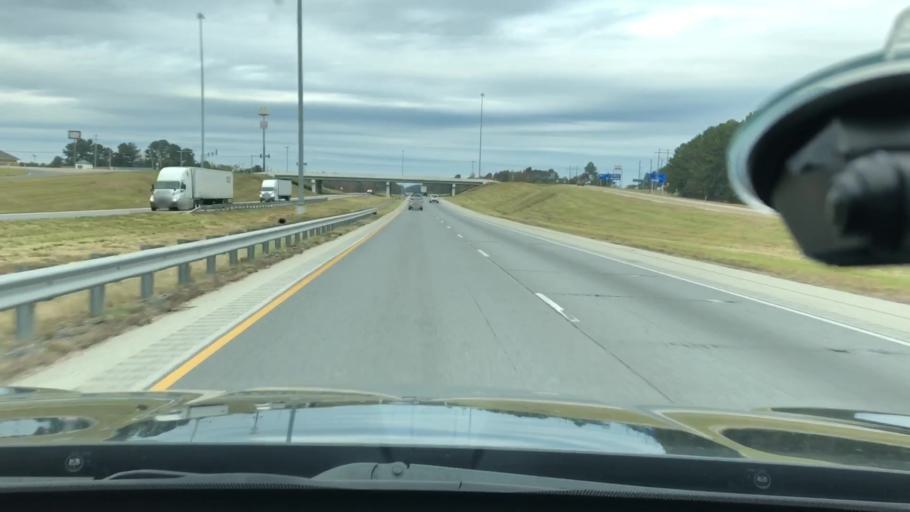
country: US
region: Arkansas
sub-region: Clark County
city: Arkadelphia
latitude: 34.1156
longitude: -93.0944
